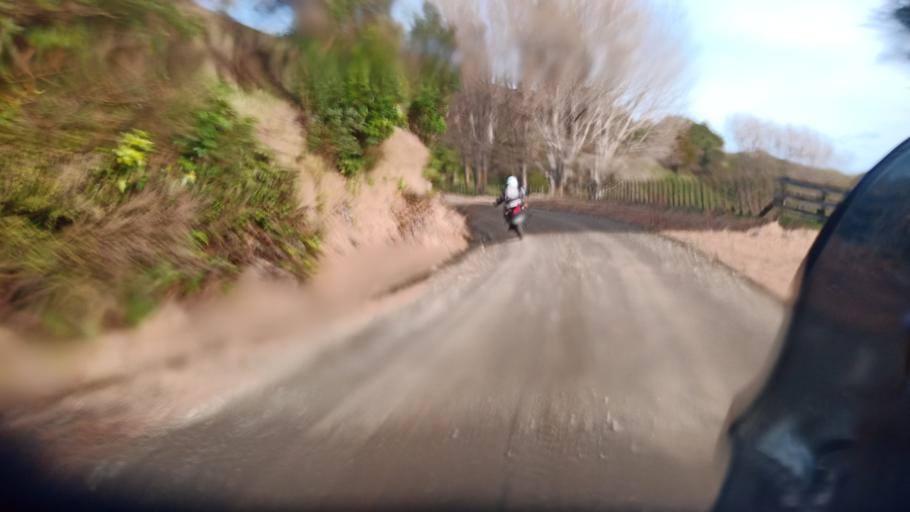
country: NZ
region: Gisborne
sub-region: Gisborne District
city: Gisborne
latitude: -38.4495
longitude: 177.5395
